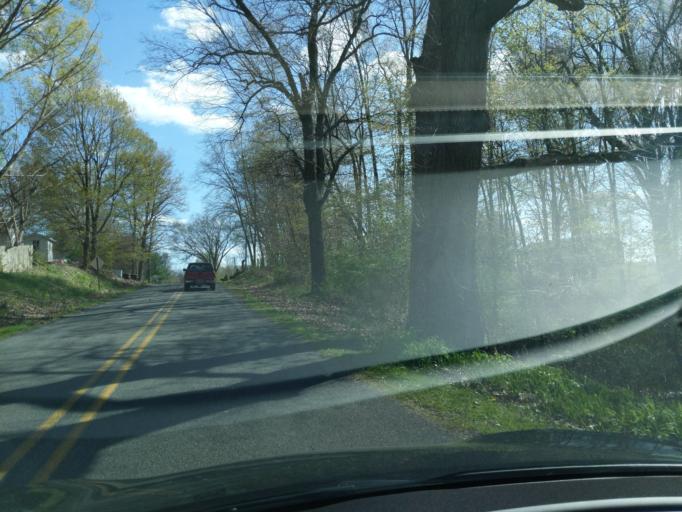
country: US
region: Michigan
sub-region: Jackson County
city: Spring Arbor
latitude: 42.3324
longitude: -84.5200
